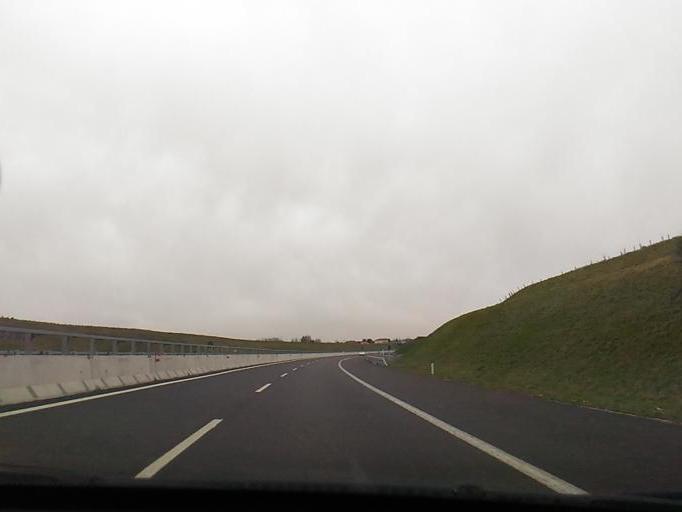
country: IT
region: Lombardy
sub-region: Provincia di Como
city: Limido Comasco
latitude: 45.6756
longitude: 8.9776
